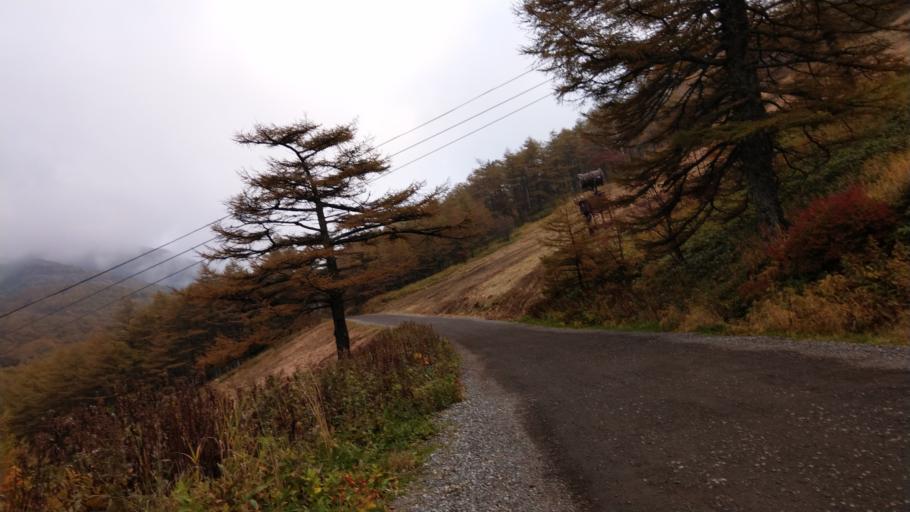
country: JP
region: Nagano
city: Komoro
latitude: 36.4069
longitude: 138.4654
